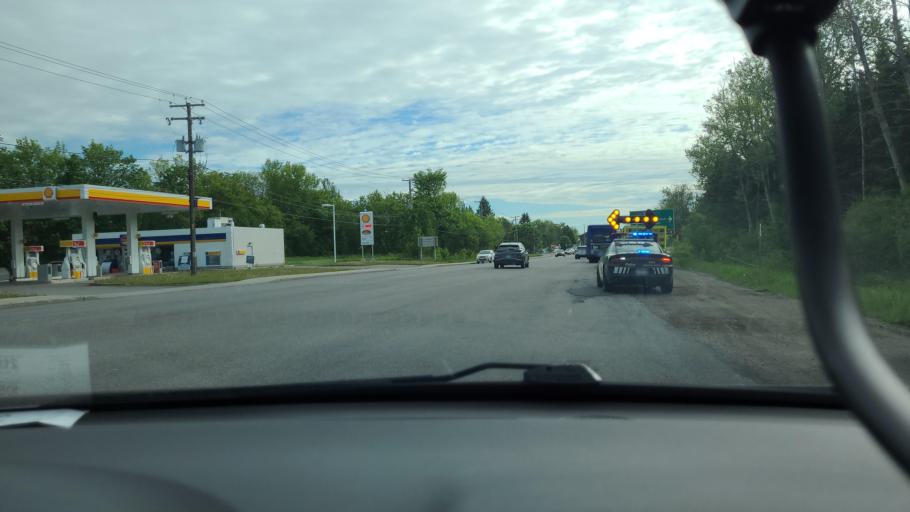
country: CA
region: Quebec
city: L'Ancienne-Lorette
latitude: 46.7665
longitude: -71.3759
